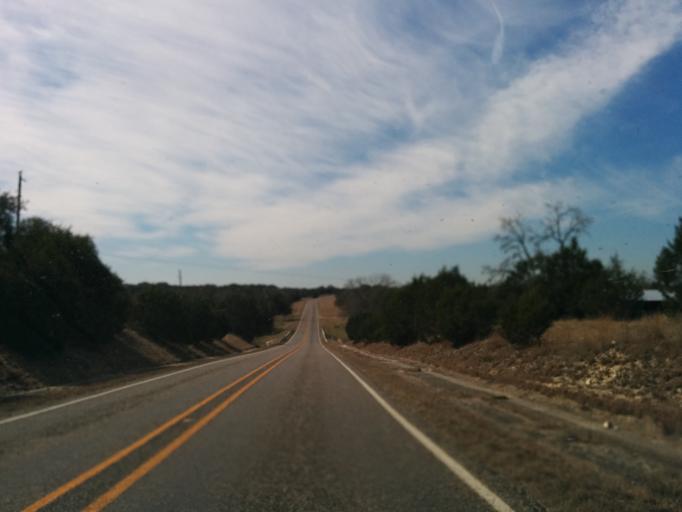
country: US
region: Texas
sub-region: Blanco County
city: Blanco
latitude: 29.9620
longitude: -98.5365
